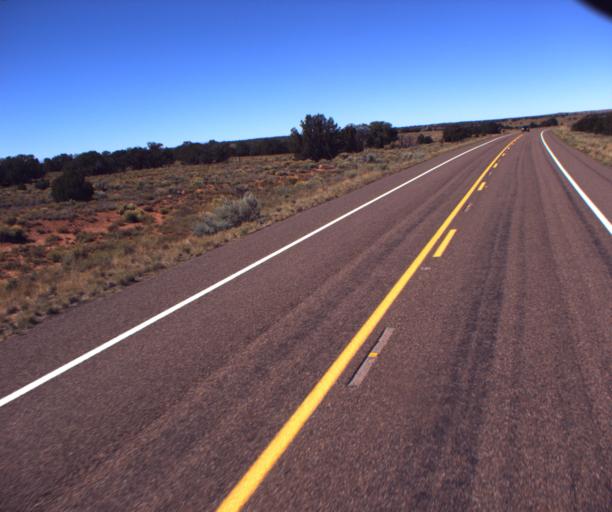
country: US
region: Arizona
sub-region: Apache County
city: Saint Johns
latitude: 34.5995
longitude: -109.6365
